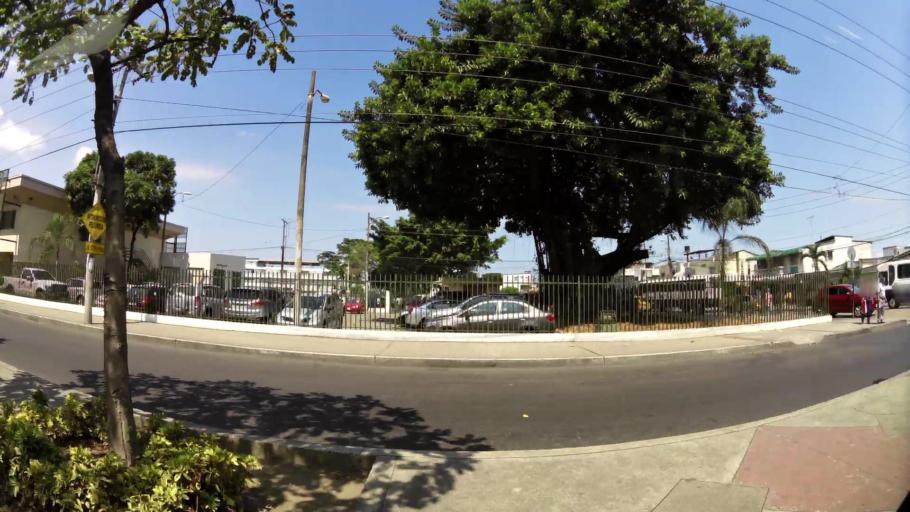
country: EC
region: Guayas
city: Guayaquil
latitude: -2.2302
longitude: -79.8995
